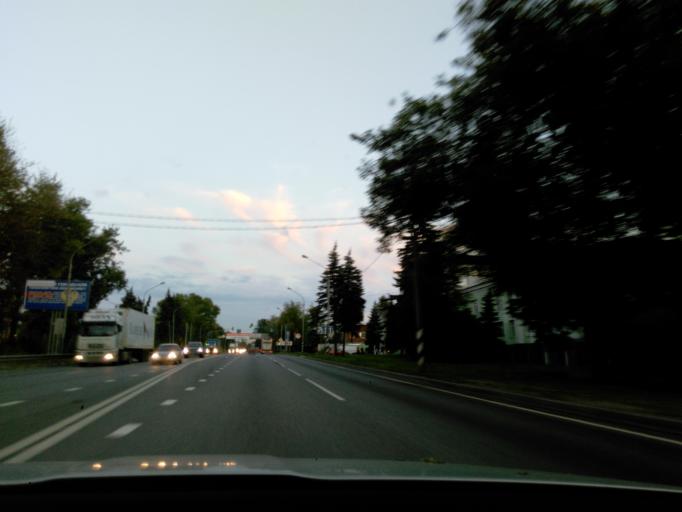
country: RU
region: Moskovskaya
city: Klin
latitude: 56.3447
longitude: 36.7097
